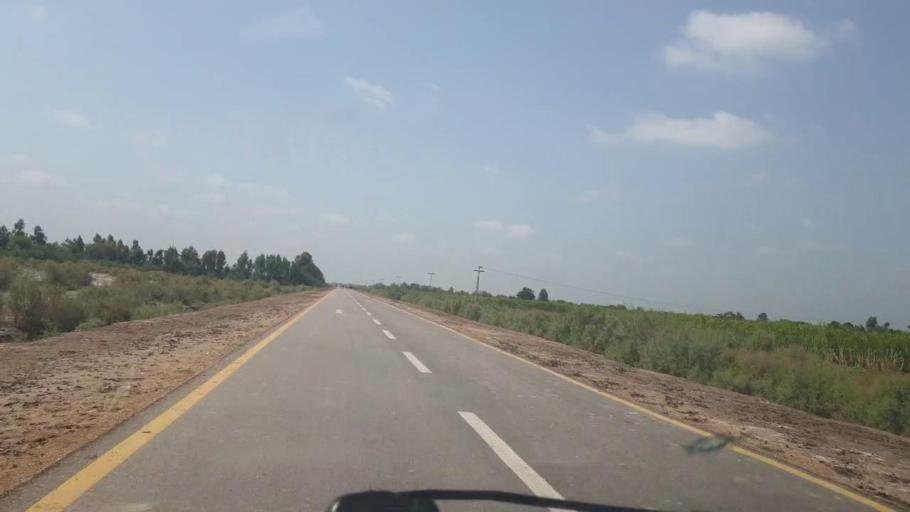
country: PK
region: Sindh
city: Berani
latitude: 25.7364
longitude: 68.9441
